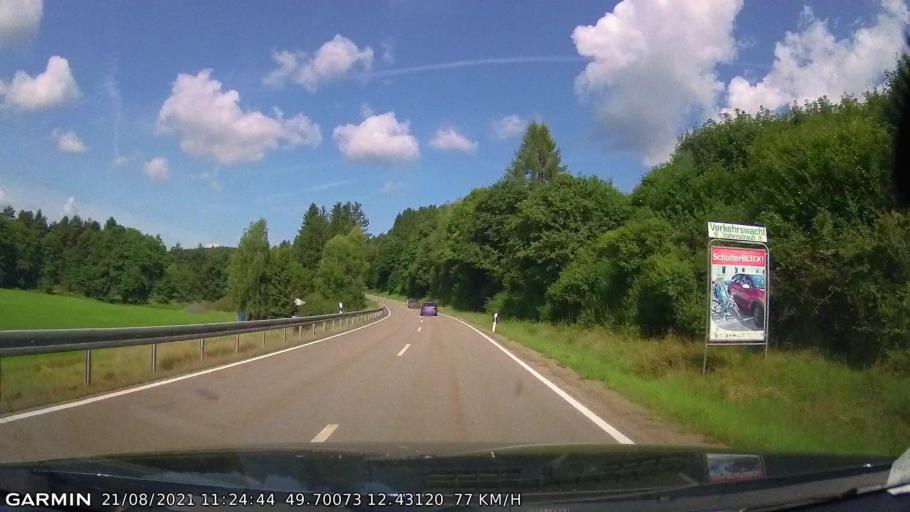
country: DE
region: Bavaria
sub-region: Upper Palatinate
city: Georgenberg
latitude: 49.7008
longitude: 12.4312
